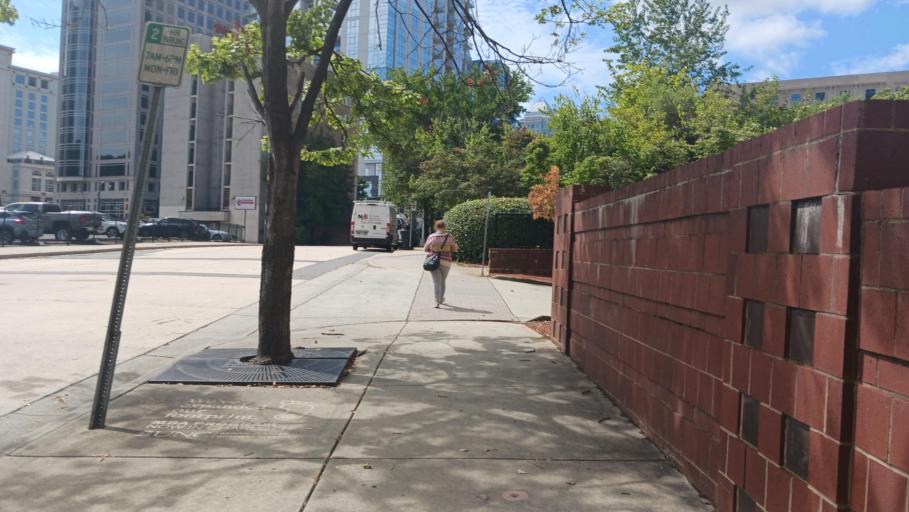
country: US
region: North Carolina
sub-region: Mecklenburg County
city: Charlotte
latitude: 35.2305
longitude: -80.8453
